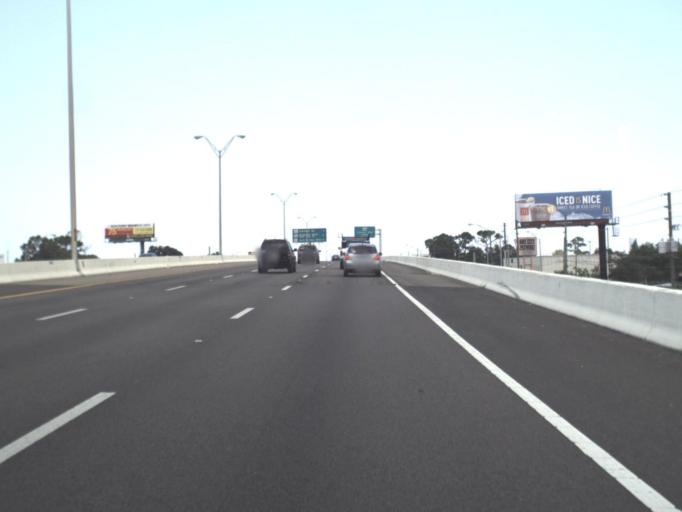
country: US
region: Florida
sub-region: Pinellas County
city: South Highpoint
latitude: 27.8846
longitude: -82.7159
